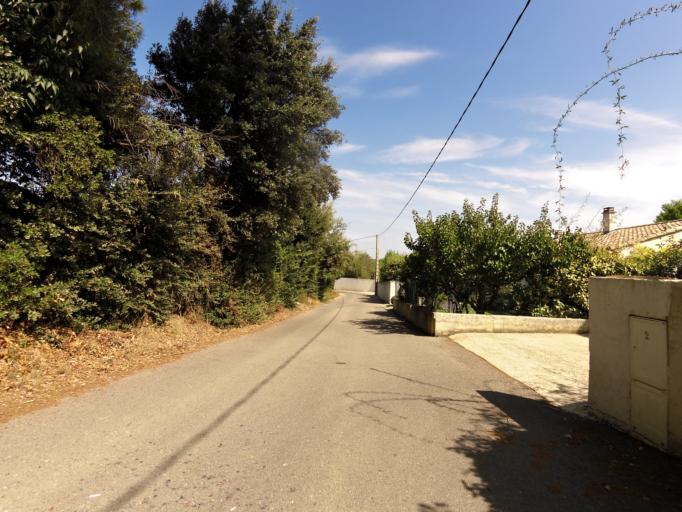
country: FR
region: Languedoc-Roussillon
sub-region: Departement du Gard
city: Mus
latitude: 43.7419
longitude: 4.2062
